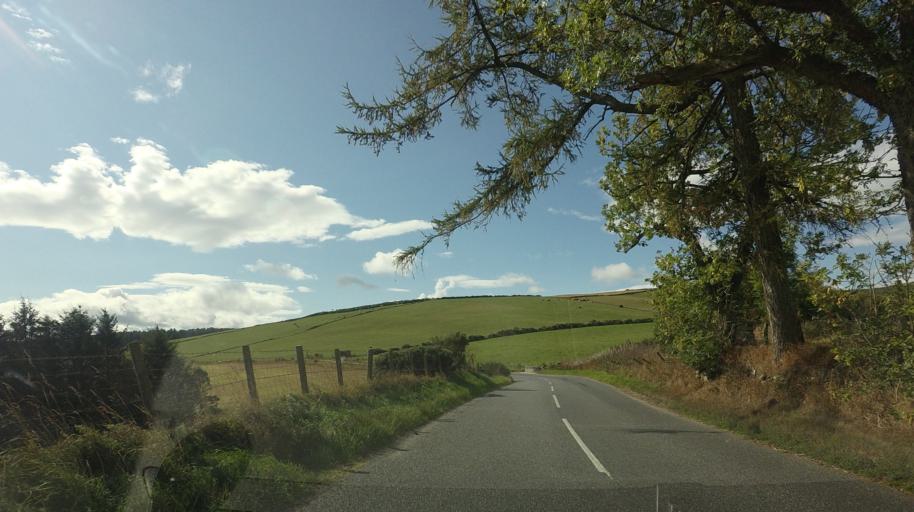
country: GB
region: Scotland
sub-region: Aberdeenshire
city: Alford
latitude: 57.2084
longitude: -2.7434
